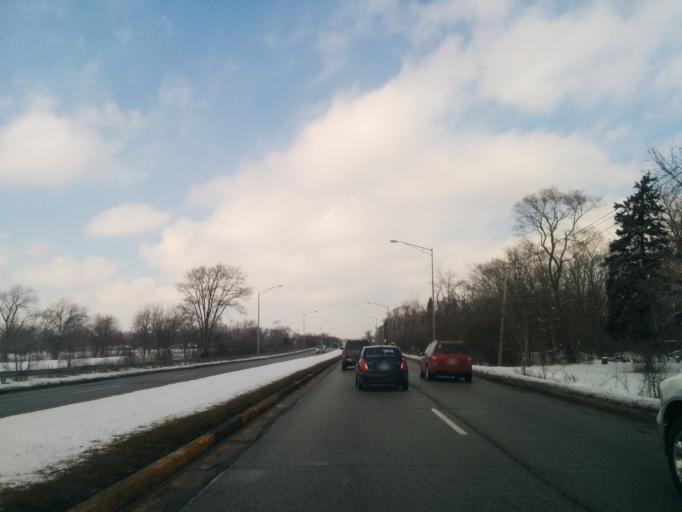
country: US
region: Illinois
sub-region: Cook County
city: Tinley Park
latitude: 41.5623
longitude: -87.7929
